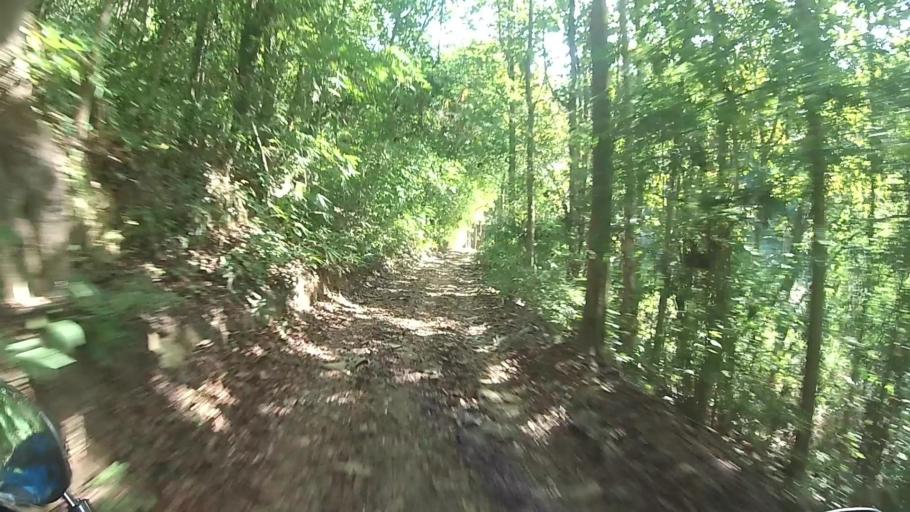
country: TH
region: Chiang Mai
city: Mae On
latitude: 19.0201
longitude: 99.3025
